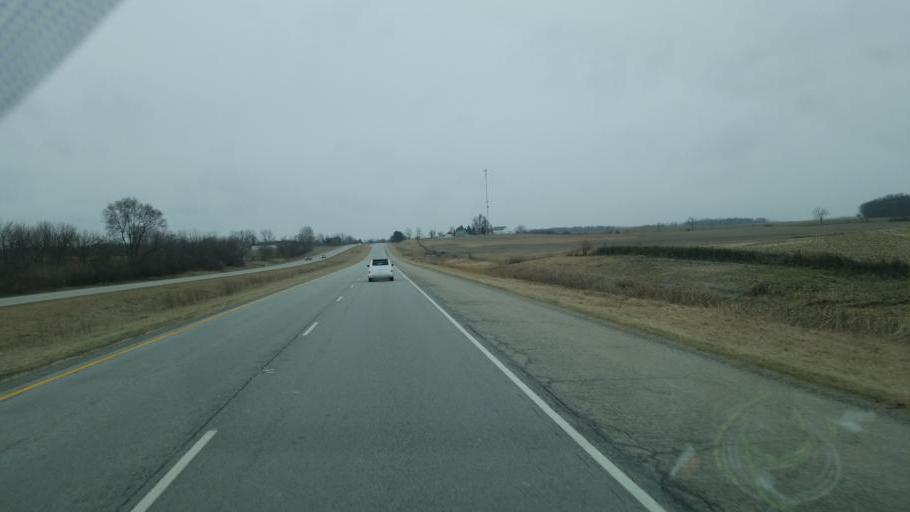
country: US
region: Indiana
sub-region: Miami County
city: Peru
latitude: 40.8931
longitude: -86.1528
